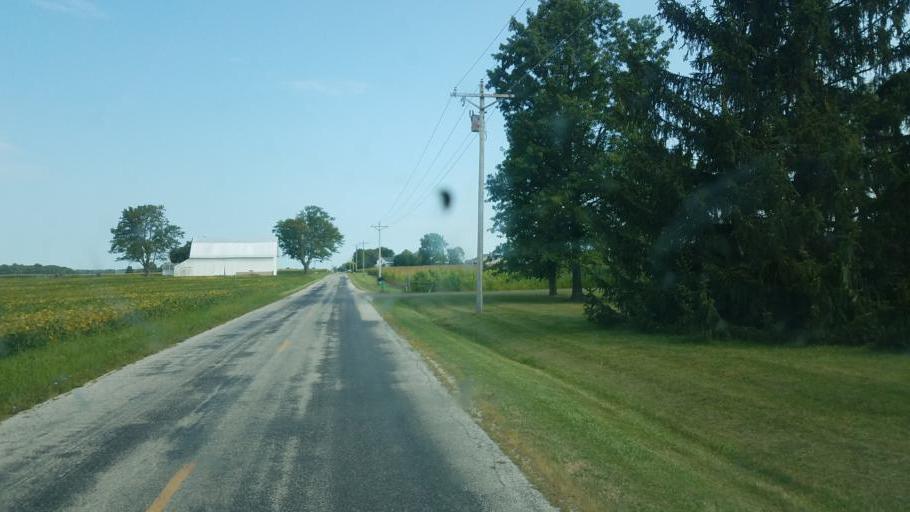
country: US
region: Ohio
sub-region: Delaware County
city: Ashley
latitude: 40.5003
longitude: -82.9956
